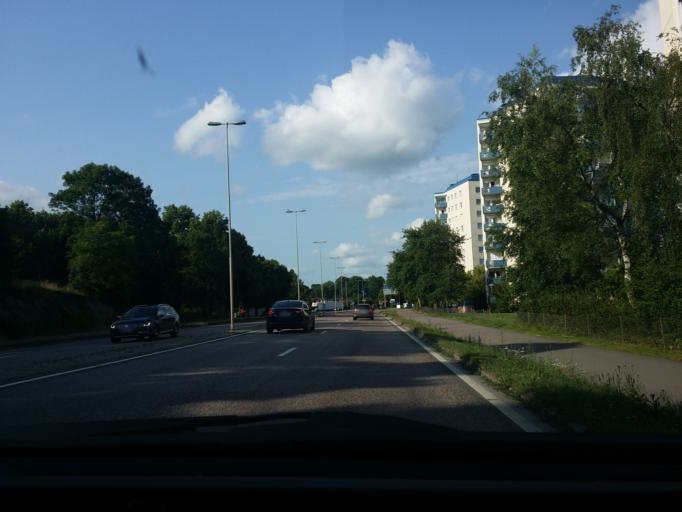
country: SE
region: Vaestmanland
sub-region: Vasteras
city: Vasteras
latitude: 59.6295
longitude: 16.5538
